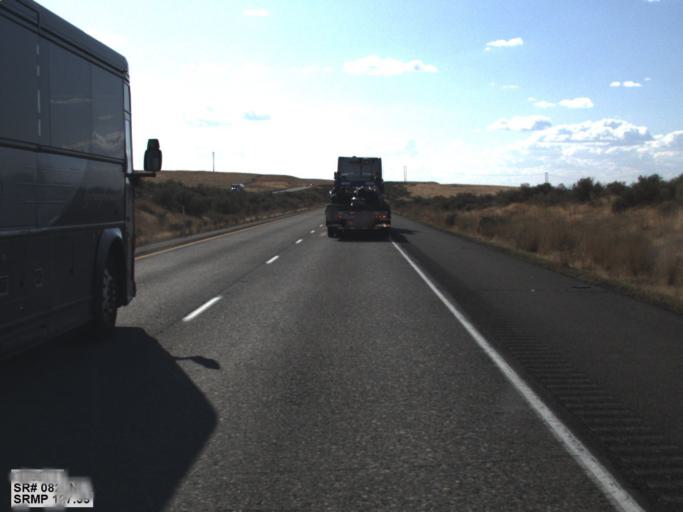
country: US
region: Oregon
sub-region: Umatilla County
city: Umatilla
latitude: 45.9891
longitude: -119.2987
